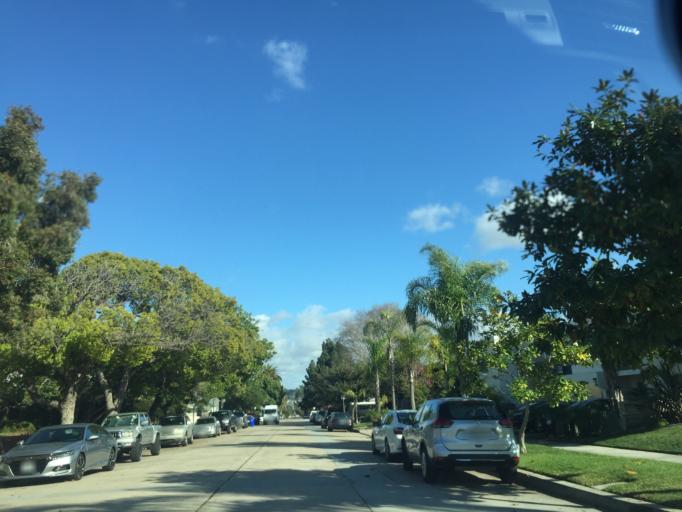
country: US
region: California
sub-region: San Diego County
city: La Jolla
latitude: 32.7964
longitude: -117.2375
